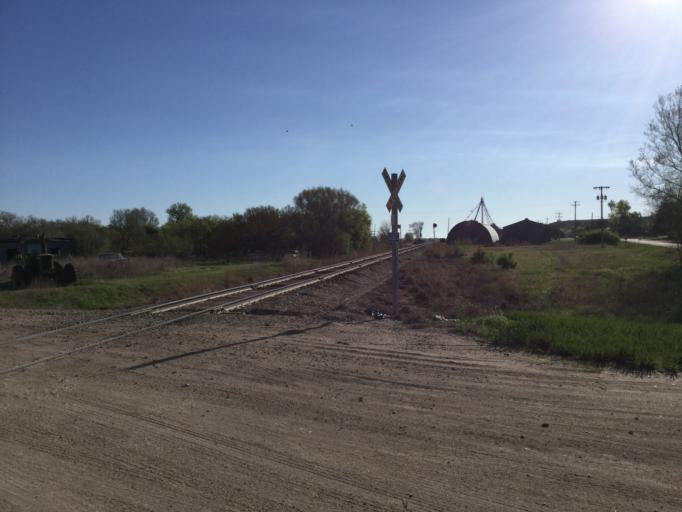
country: US
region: Kansas
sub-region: Norton County
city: Norton
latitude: 39.7374
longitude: -100.1802
